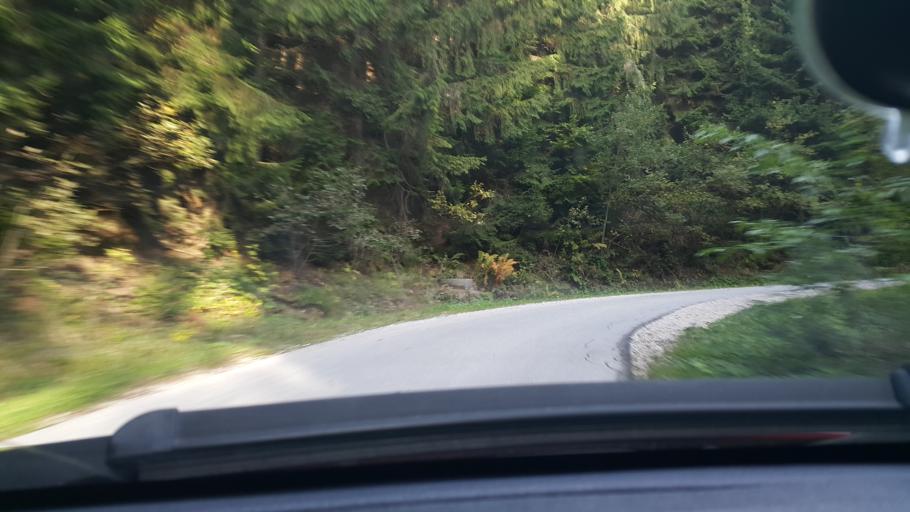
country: SI
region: Mislinja
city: Mislinja
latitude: 46.4268
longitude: 15.2633
